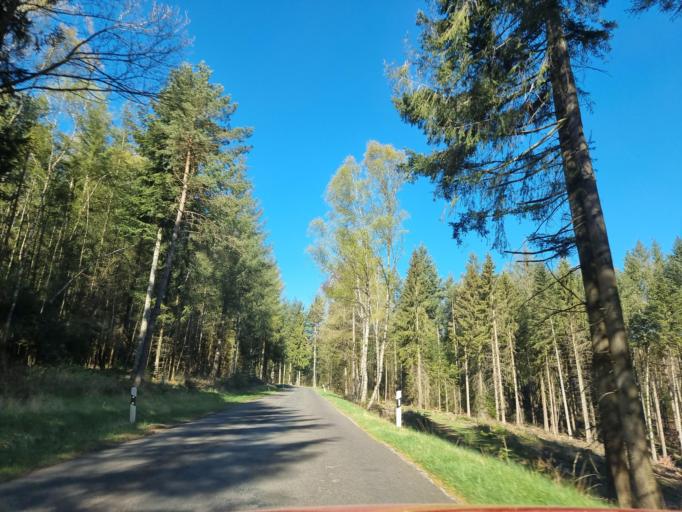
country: DE
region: Rheinland-Pfalz
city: Heckenmunster
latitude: 49.8897
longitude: 6.7728
